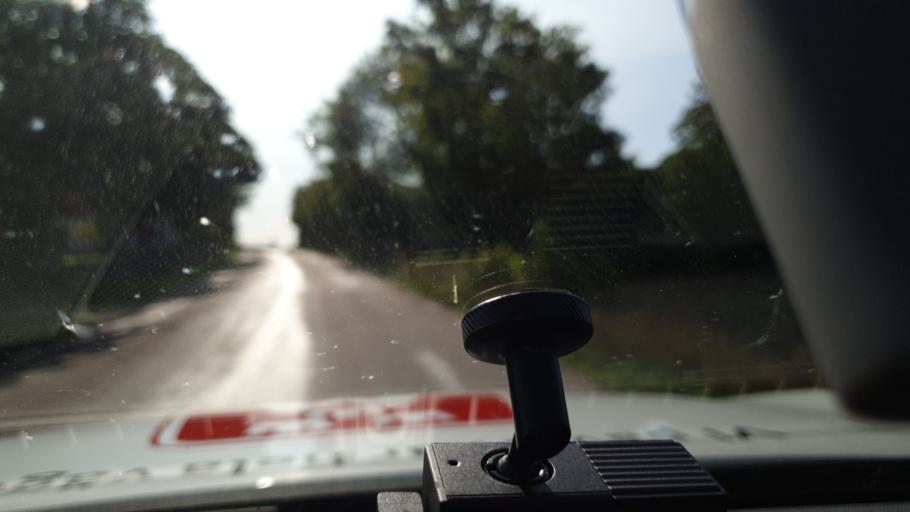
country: SE
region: Gotland
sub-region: Gotland
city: Hemse
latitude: 57.1518
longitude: 18.2825
